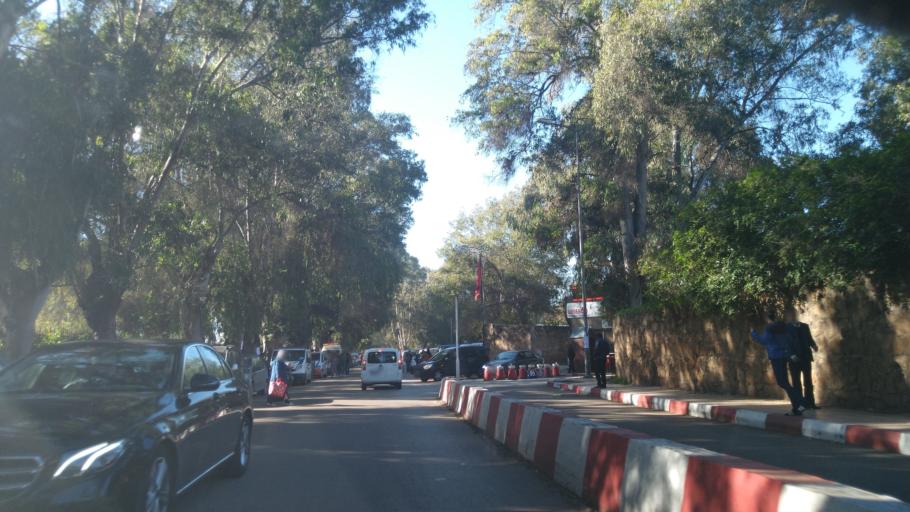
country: MA
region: Rabat-Sale-Zemmour-Zaer
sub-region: Rabat
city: Rabat
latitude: 33.9839
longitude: -6.8491
